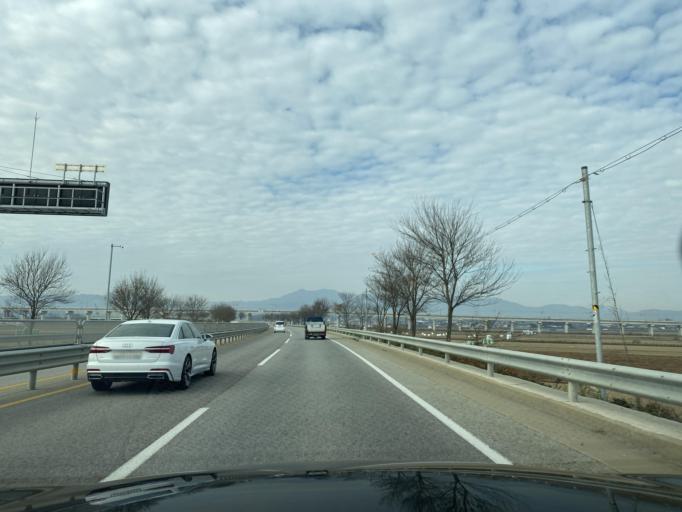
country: KR
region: Chungcheongnam-do
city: Yesan
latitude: 36.6927
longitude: 126.7310
